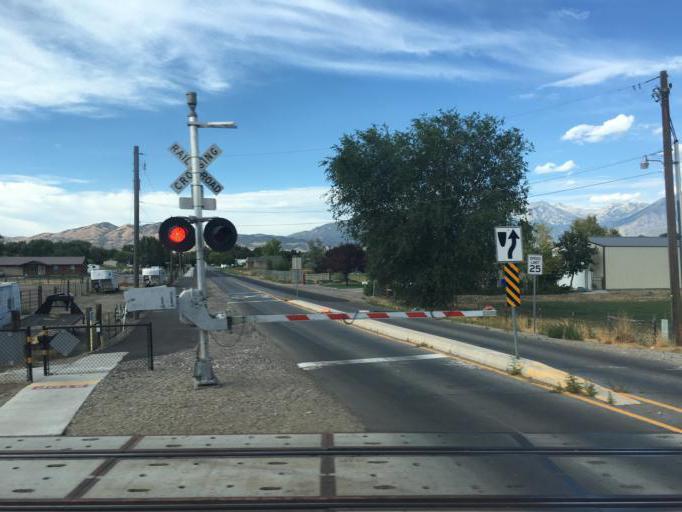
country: US
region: Utah
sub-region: Utah County
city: Lehi
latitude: 40.3808
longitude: -111.8493
